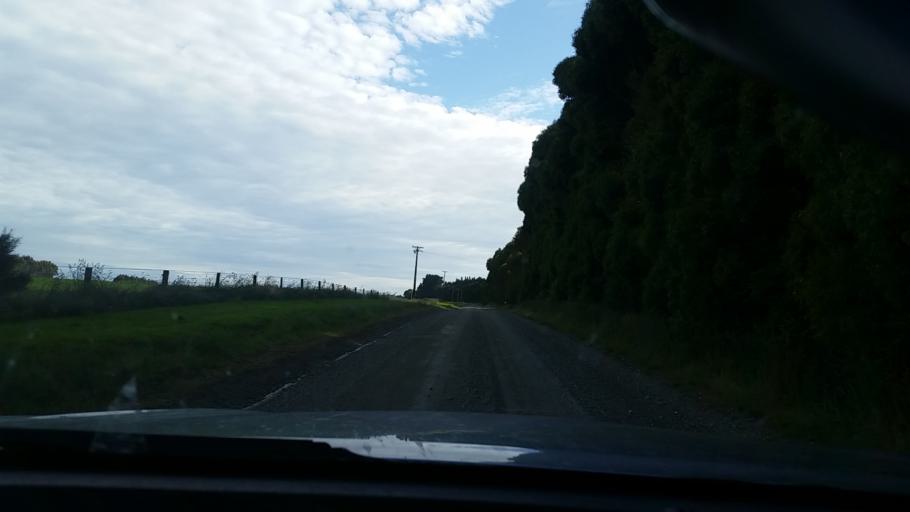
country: NZ
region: Southland
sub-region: Gore District
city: Gore
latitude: -46.2572
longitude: 168.7433
